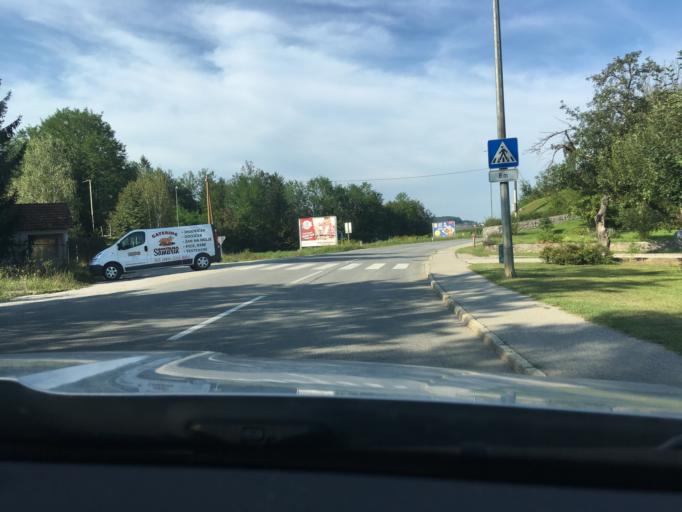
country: SI
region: Crnomelj
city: Crnomelj
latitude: 45.5643
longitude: 15.1724
